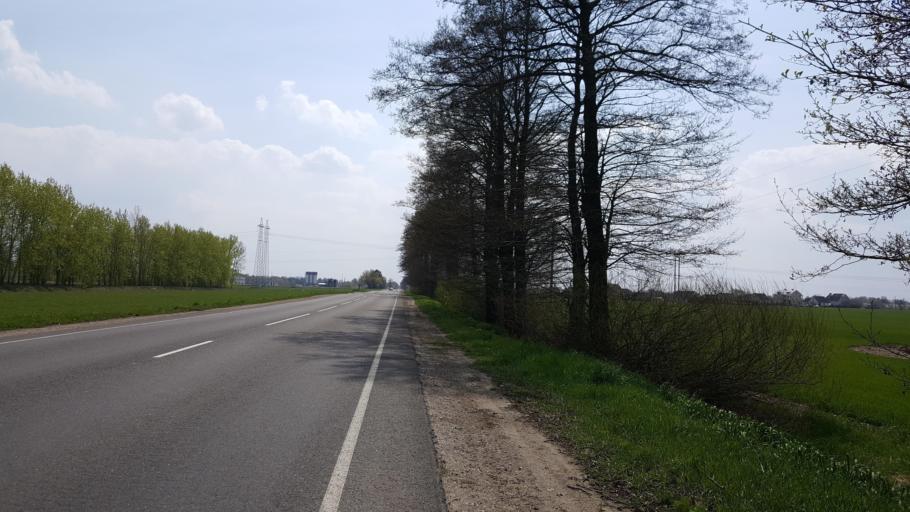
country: BY
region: Brest
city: Zhabinka
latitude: 52.2148
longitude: 23.9972
